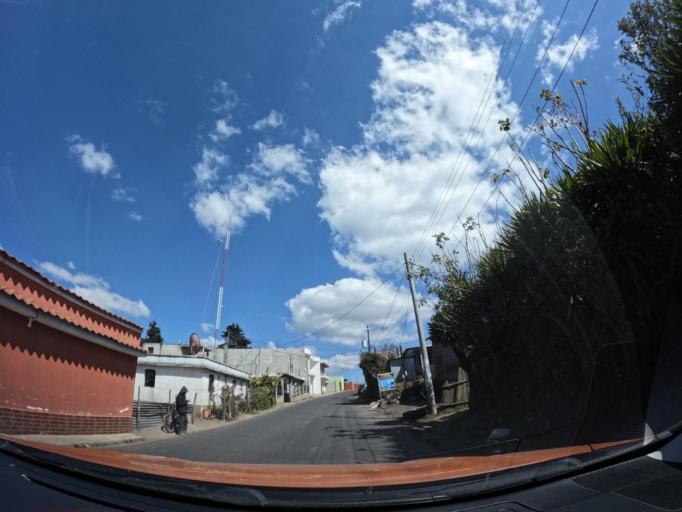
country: GT
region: Chimaltenango
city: Patzun
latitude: 14.6475
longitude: -91.0390
